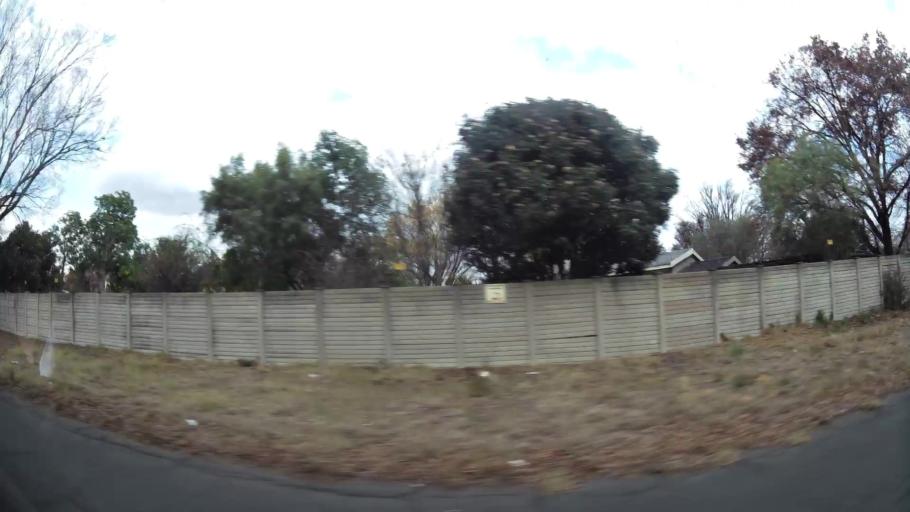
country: ZA
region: Orange Free State
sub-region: Fezile Dabi District Municipality
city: Sasolburg
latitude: -26.7917
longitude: 27.8161
